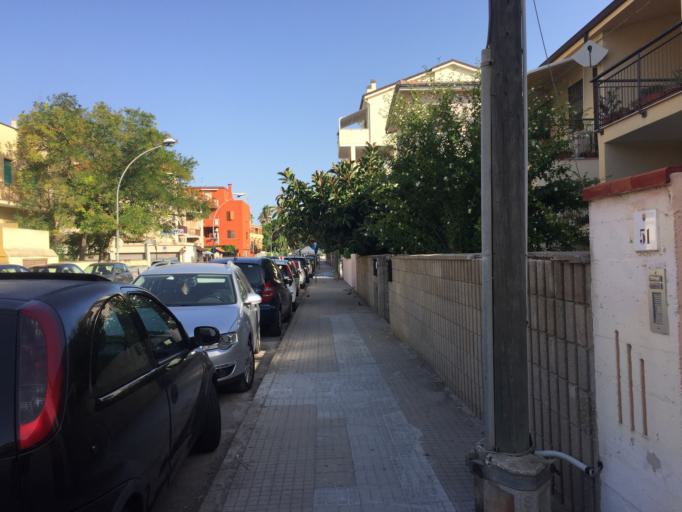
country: IT
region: Sardinia
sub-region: Provincia di Sassari
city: Alghero
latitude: 40.5756
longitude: 8.3173
